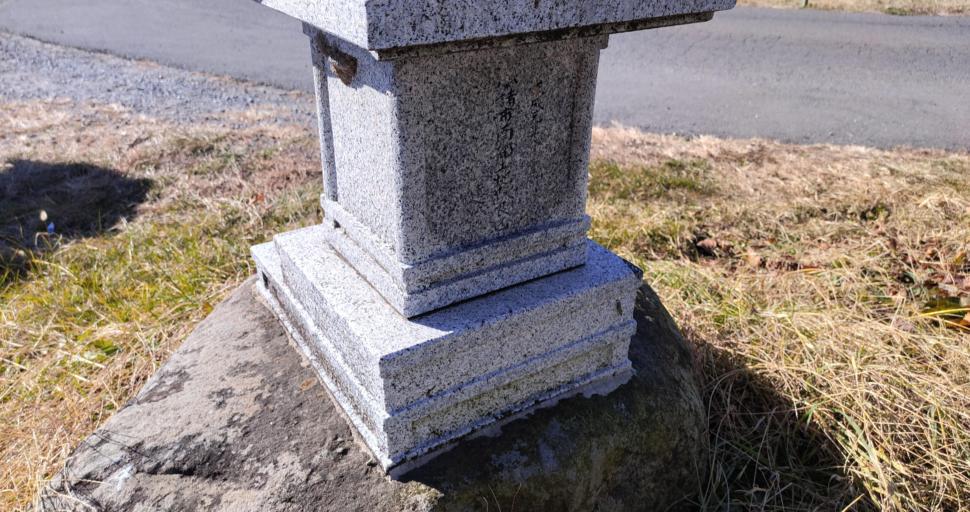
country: JP
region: Nagano
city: Komoro
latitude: 36.2860
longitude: 138.4488
